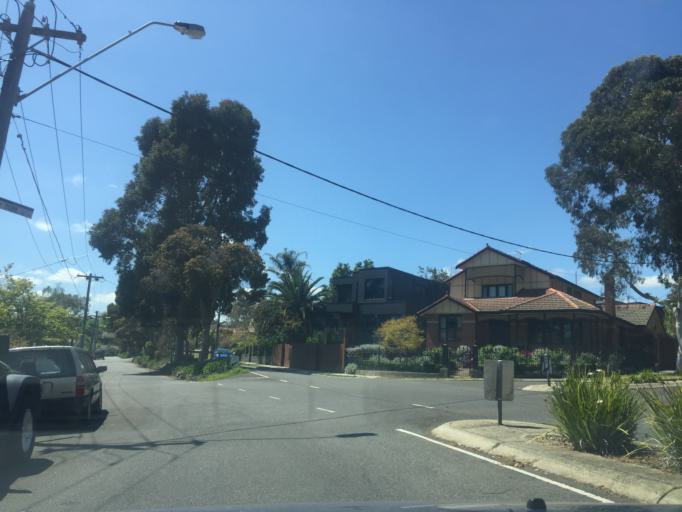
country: AU
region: Victoria
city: Ivanhoe East
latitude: -37.7702
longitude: 145.0519
